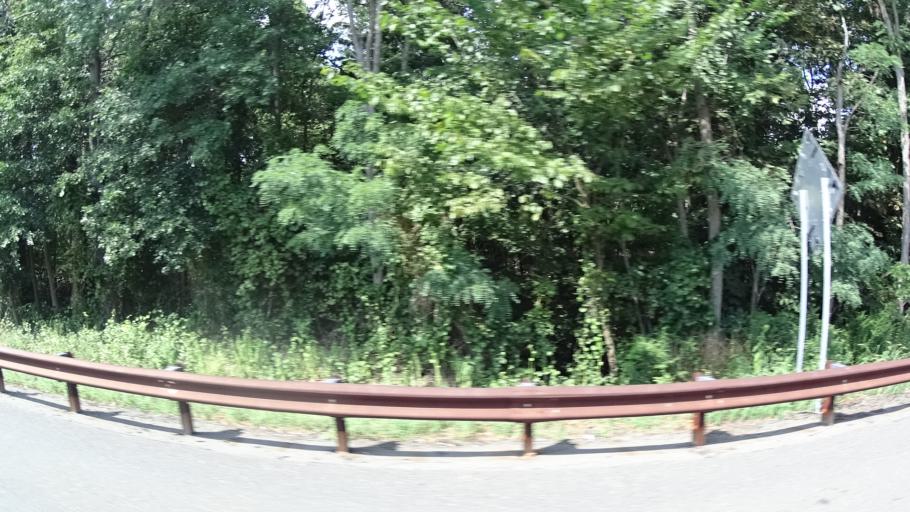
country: US
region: New Jersey
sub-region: Monmouth County
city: Tinton Falls
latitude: 40.3010
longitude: -74.0936
